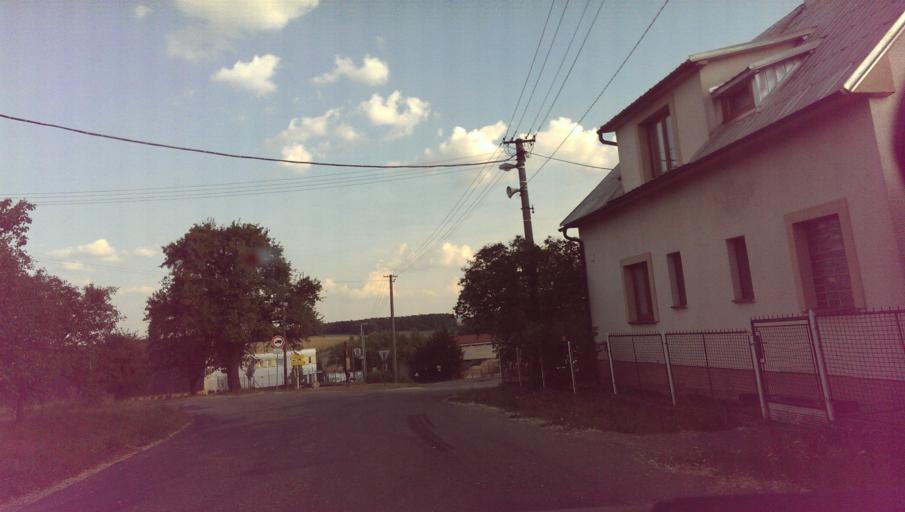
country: CZ
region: Zlin
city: Hvozdna
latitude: 49.2564
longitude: 17.7569
